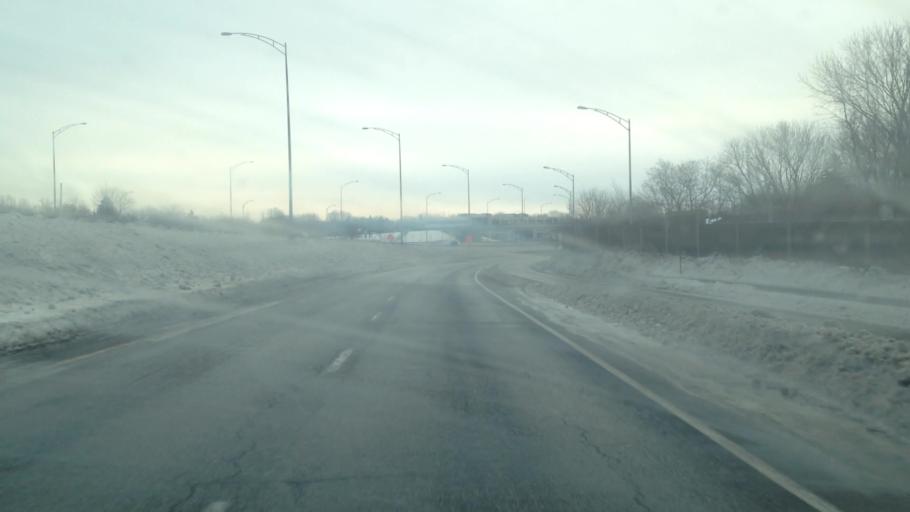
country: CA
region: Quebec
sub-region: Monteregie
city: Brossard
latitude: 45.4643
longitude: -73.4620
